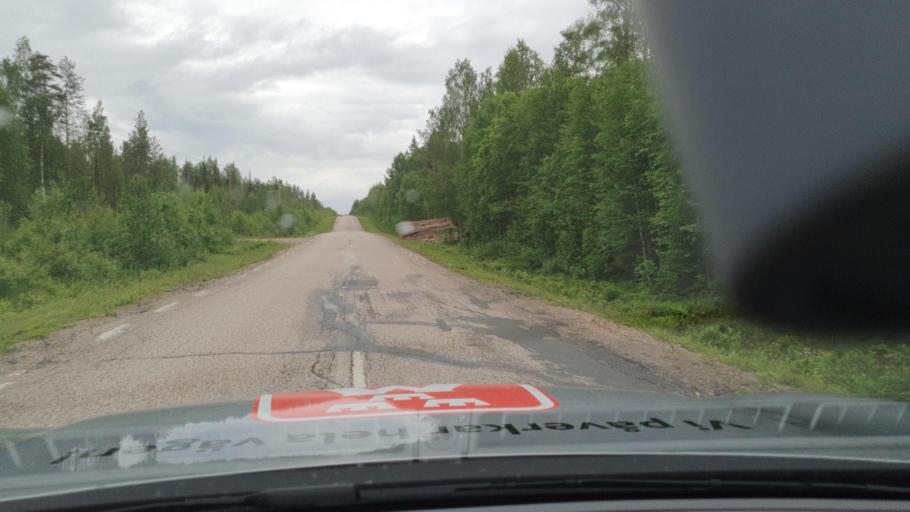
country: SE
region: Norrbotten
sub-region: Overkalix Kommun
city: OEverkalix
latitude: 66.4086
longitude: 22.7874
